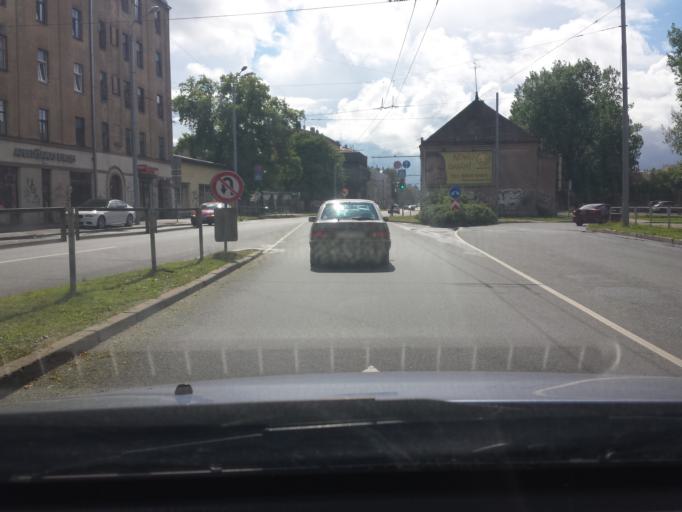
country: LV
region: Riga
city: Riga
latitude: 56.9619
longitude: 24.1467
